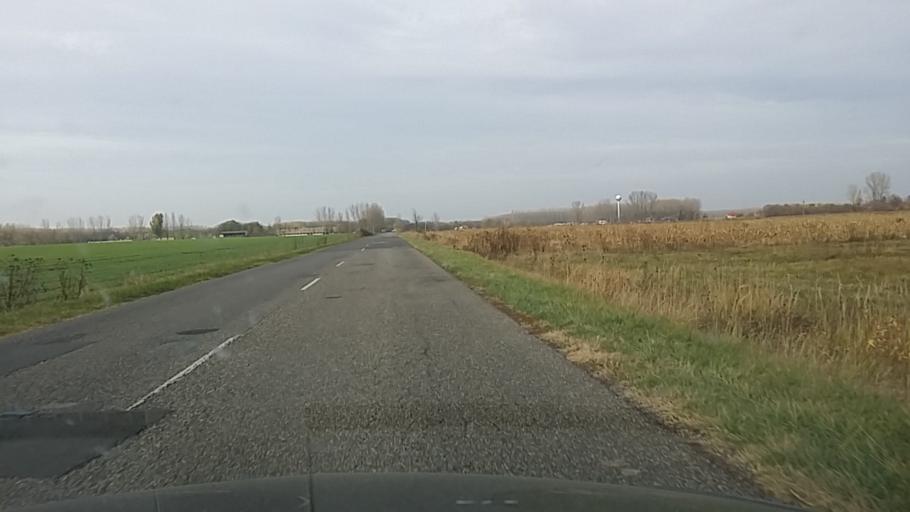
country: HU
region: Szabolcs-Szatmar-Bereg
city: Nyirbogdany
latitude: 48.0528
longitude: 21.8614
